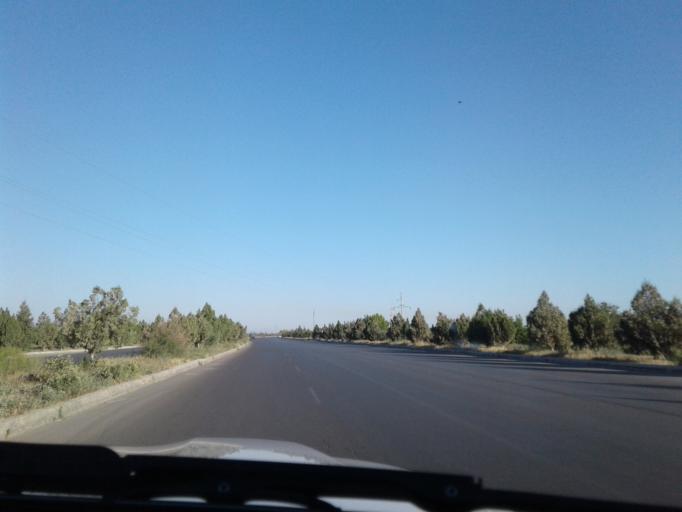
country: TM
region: Ahal
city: Abadan
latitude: 38.0943
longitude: 58.1979
